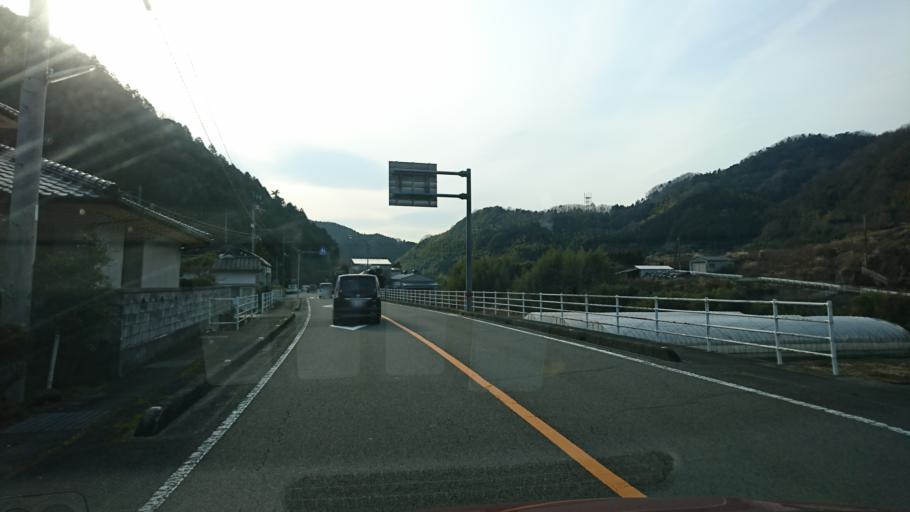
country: JP
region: Ehime
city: Hojo
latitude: 33.8999
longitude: 132.8674
